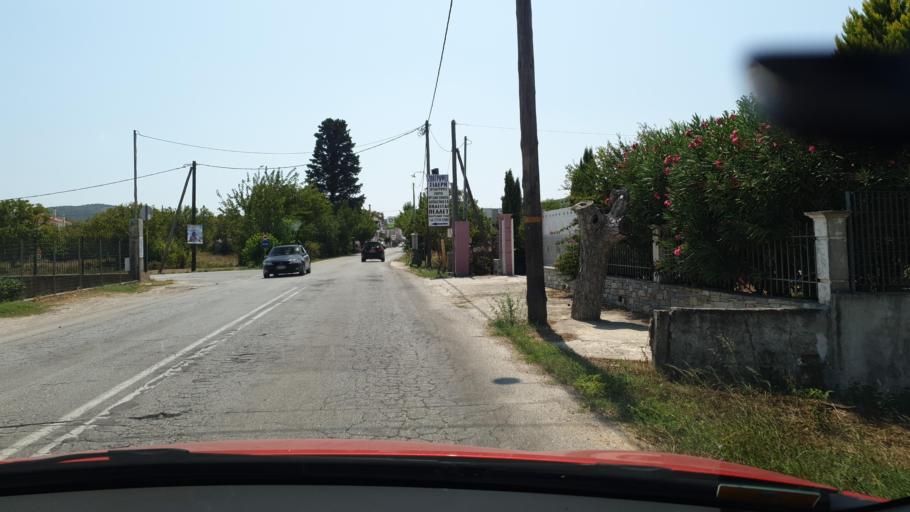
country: GR
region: Central Greece
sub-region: Nomos Evvoias
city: Oxilithos
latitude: 38.5028
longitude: 24.1101
